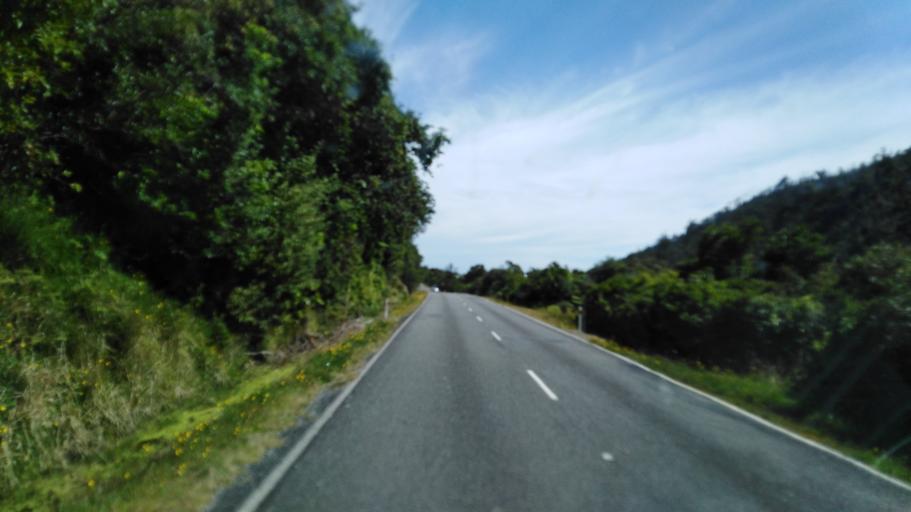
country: NZ
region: West Coast
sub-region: Buller District
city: Westport
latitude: -41.5320
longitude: 171.9534
